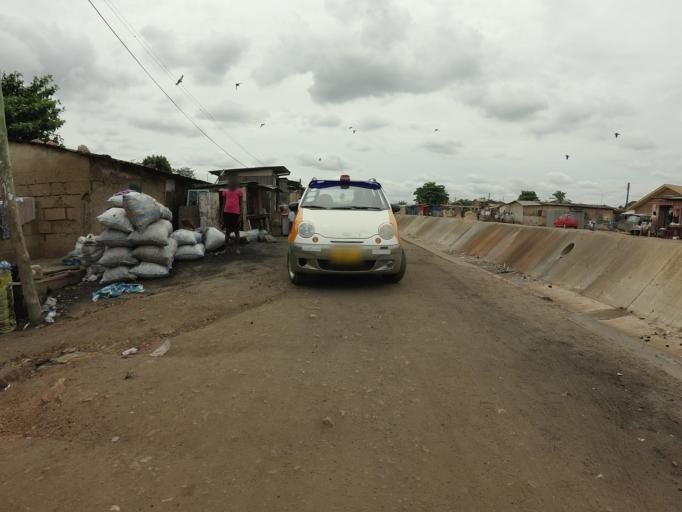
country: GH
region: Greater Accra
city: Accra
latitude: 5.5917
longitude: -0.2140
